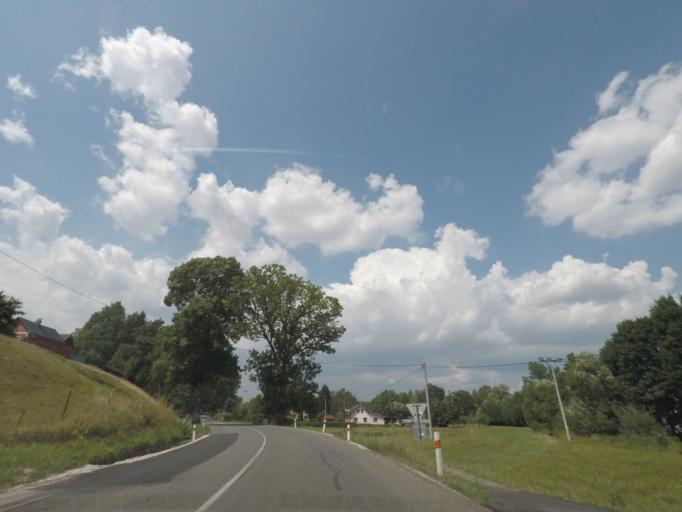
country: CZ
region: Kralovehradecky
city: Zadni Mostek
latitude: 50.5357
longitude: 15.6744
